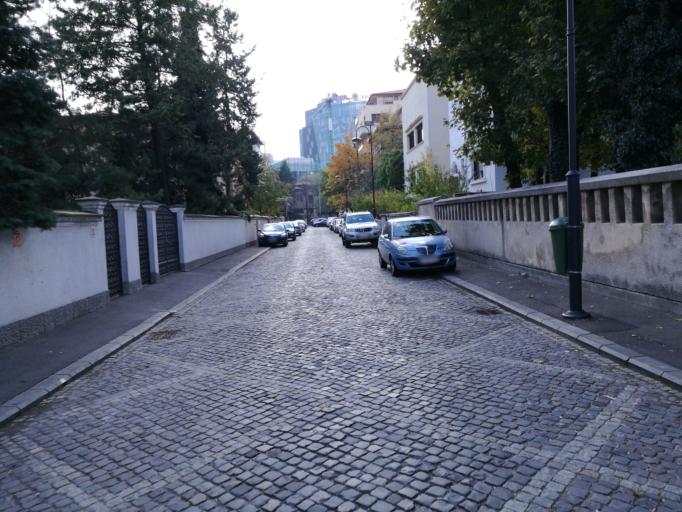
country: RO
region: Bucuresti
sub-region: Municipiul Bucuresti
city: Bucharest
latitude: 44.4680
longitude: 26.0882
